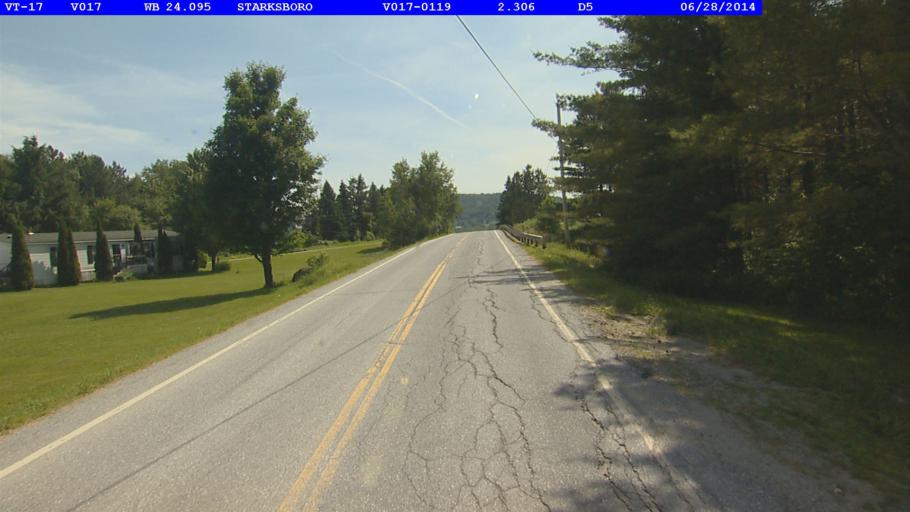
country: US
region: Vermont
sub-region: Addison County
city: Bristol
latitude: 44.1756
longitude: -72.9792
